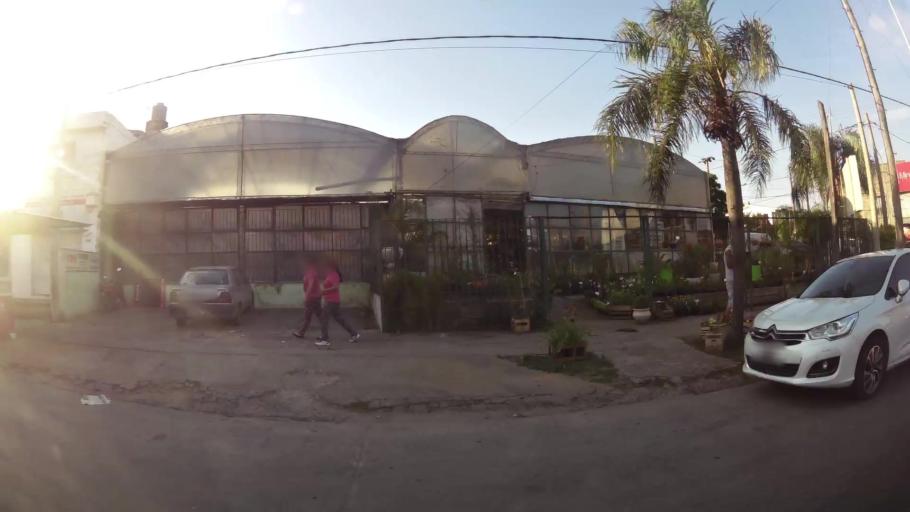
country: AR
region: Cordoba
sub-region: Departamento de Capital
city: Cordoba
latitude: -31.3869
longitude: -64.2278
